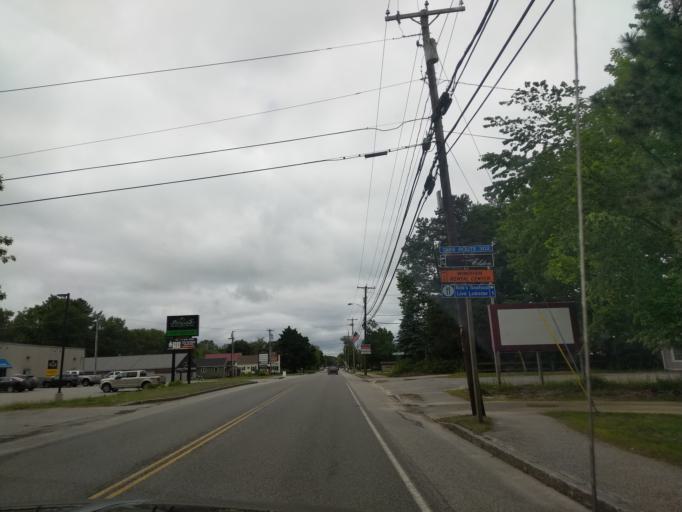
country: US
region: Maine
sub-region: Cumberland County
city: North Windham
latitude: 43.8355
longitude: -70.4326
